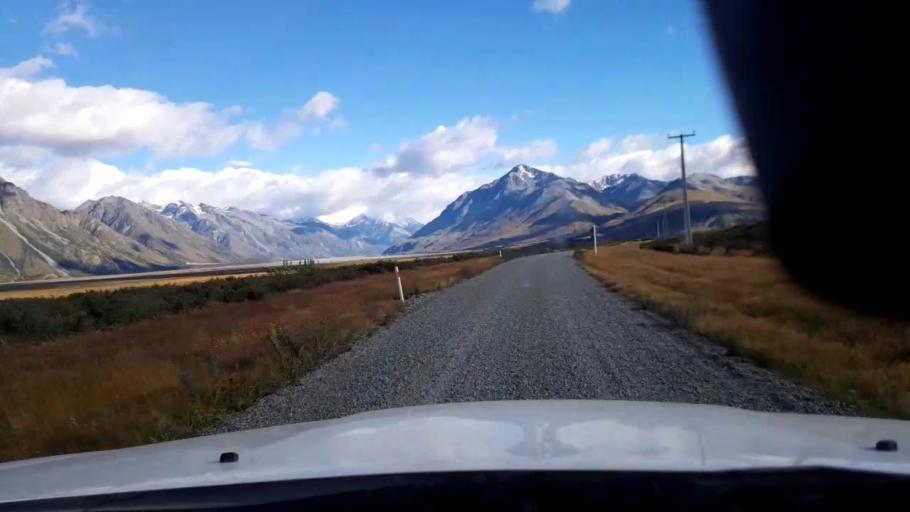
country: NZ
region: Canterbury
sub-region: Timaru District
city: Pleasant Point
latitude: -43.7625
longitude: 170.5698
